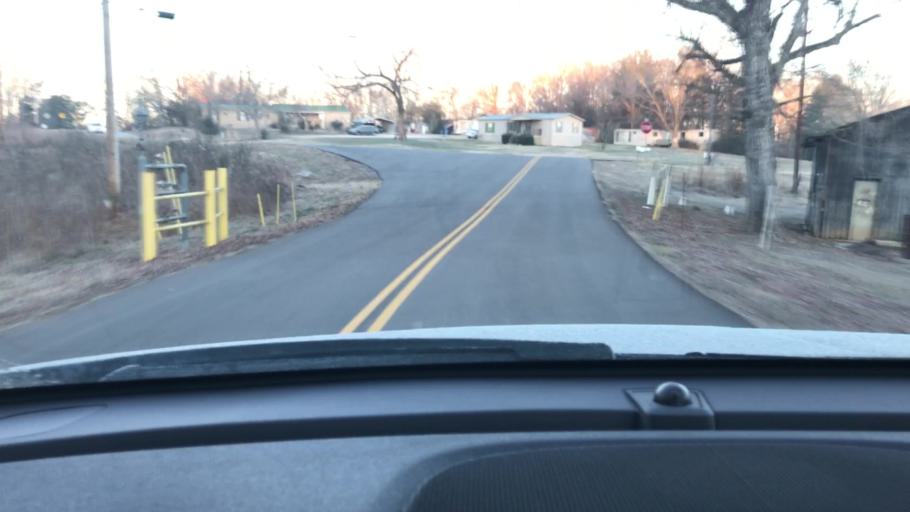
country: US
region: Tennessee
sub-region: Dickson County
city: Charlotte
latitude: 36.2112
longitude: -87.2605
